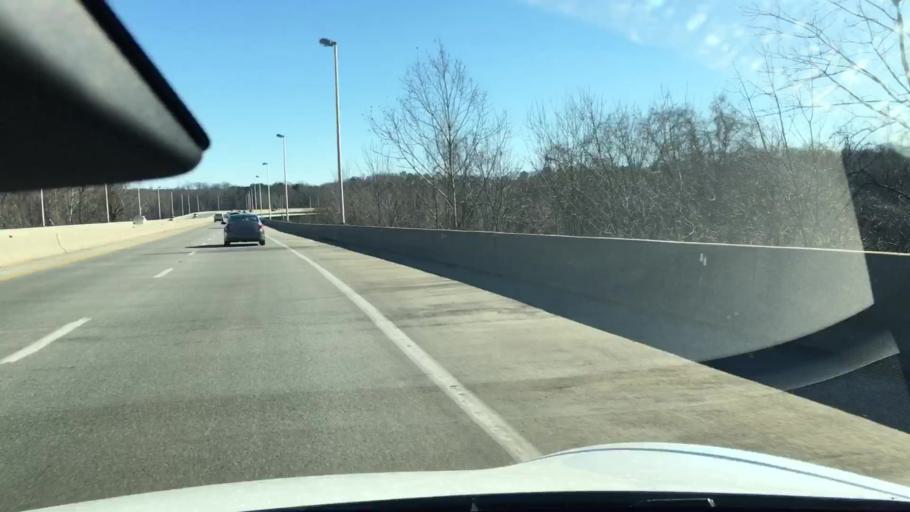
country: US
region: Virginia
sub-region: Henrico County
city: Tuckahoe
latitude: 37.5624
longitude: -77.5756
